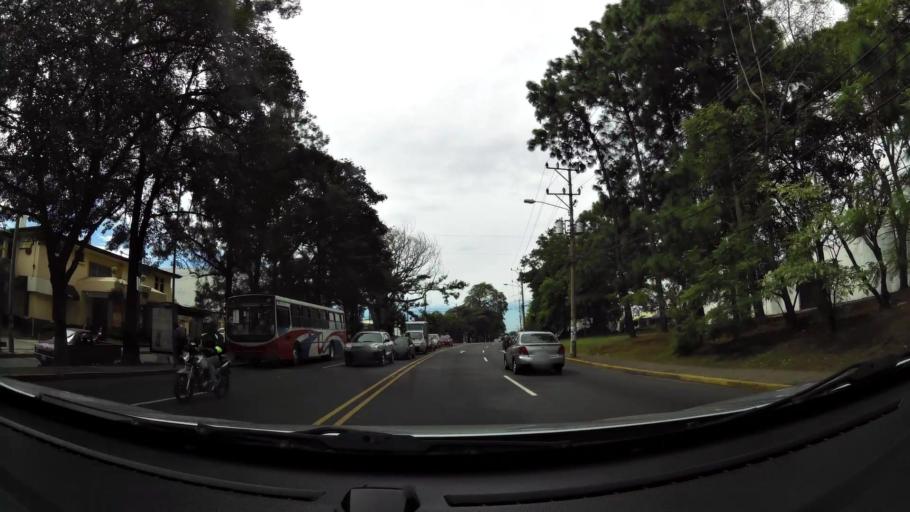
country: CR
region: San Jose
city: San Pedro
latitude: 9.9324
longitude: -84.0581
